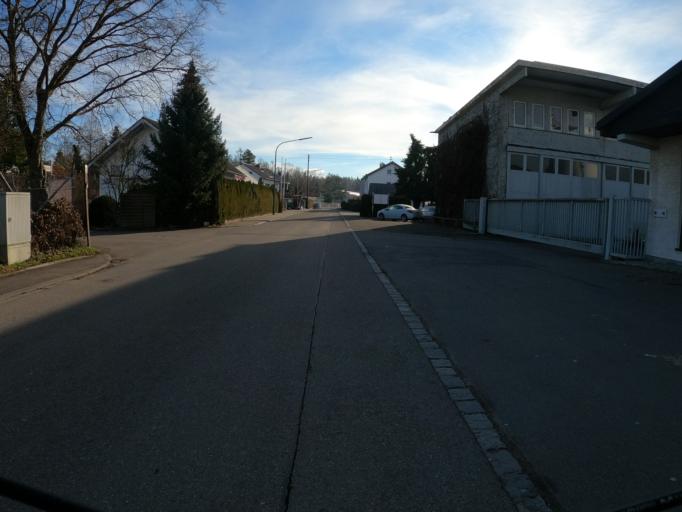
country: DE
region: Bavaria
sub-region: Swabia
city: Nersingen
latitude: 48.4184
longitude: 10.1539
